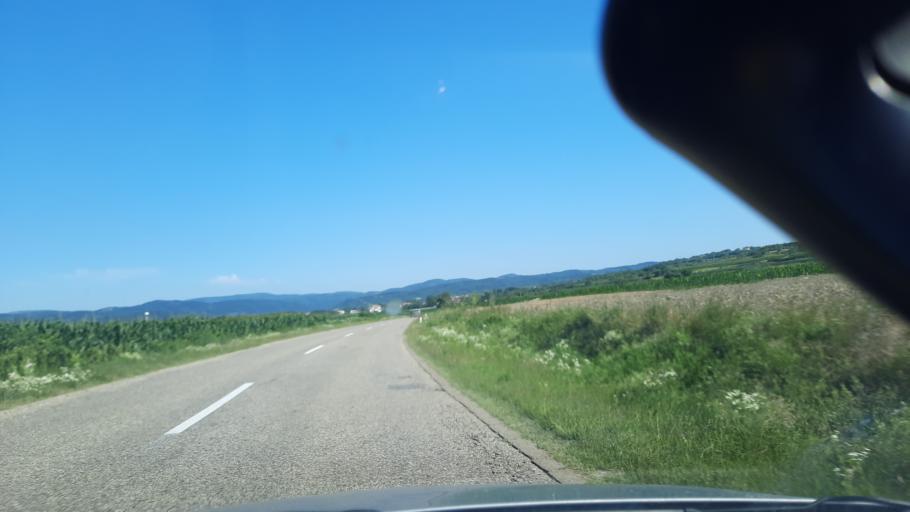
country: RS
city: Turija
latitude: 44.5606
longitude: 21.5348
